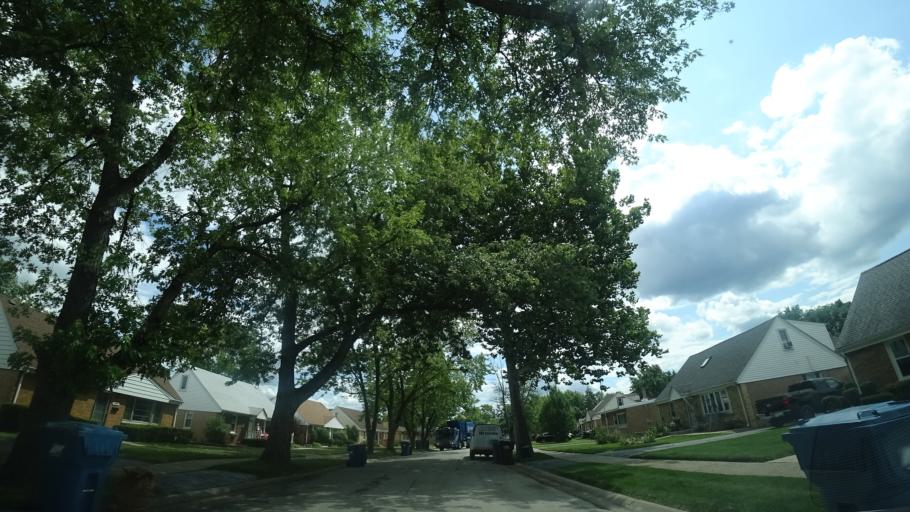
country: US
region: Illinois
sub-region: Cook County
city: Alsip
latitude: 41.6822
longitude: -87.7334
